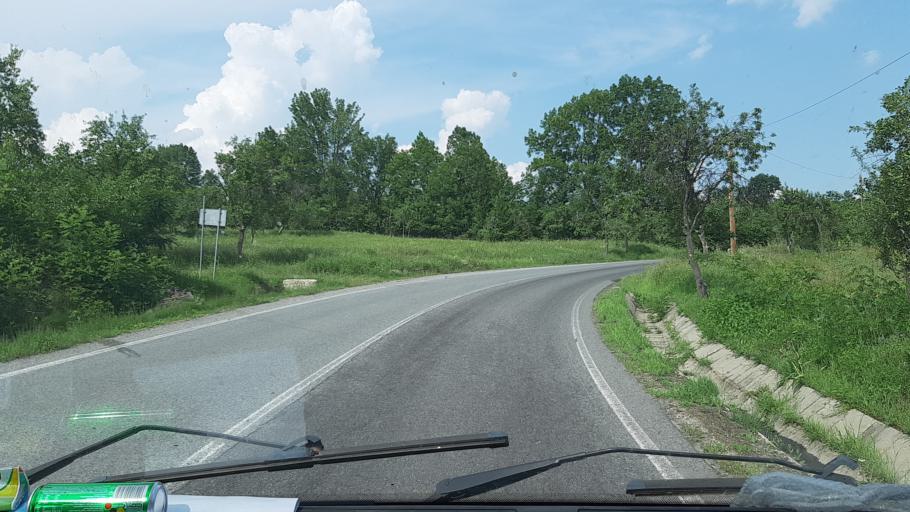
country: RO
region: Caras-Severin
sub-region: Comuna Farliug
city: Farliug
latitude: 45.5137
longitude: 21.8745
